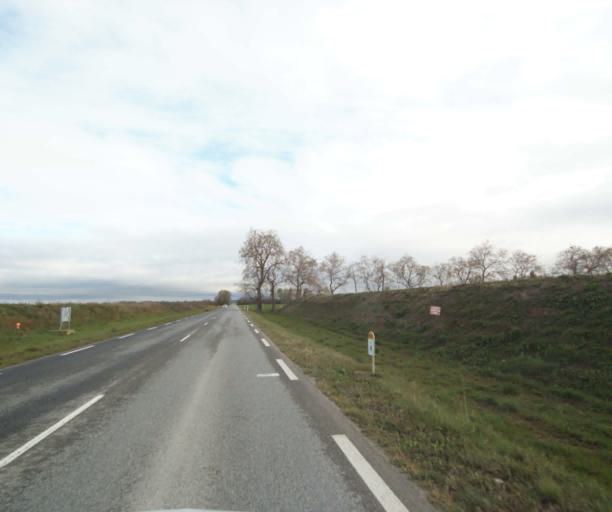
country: FR
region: Midi-Pyrenees
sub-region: Departement de l'Ariege
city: Saverdun
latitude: 43.2125
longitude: 1.6080
